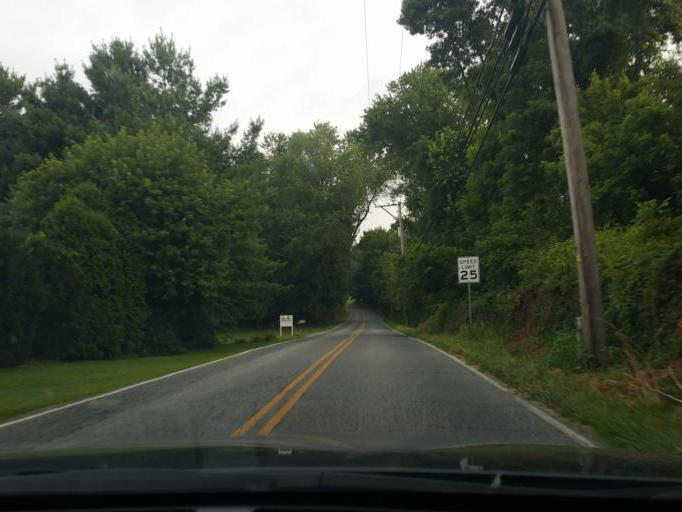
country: US
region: Maryland
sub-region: Cecil County
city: Rising Sun
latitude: 39.6723
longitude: -76.1558
